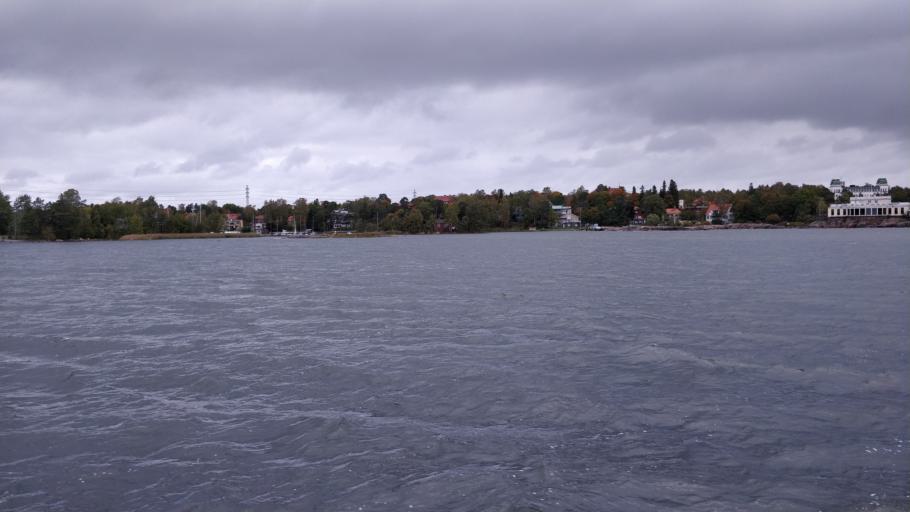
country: FI
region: Uusimaa
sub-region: Helsinki
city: Helsinki
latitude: 60.1780
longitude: 25.0026
